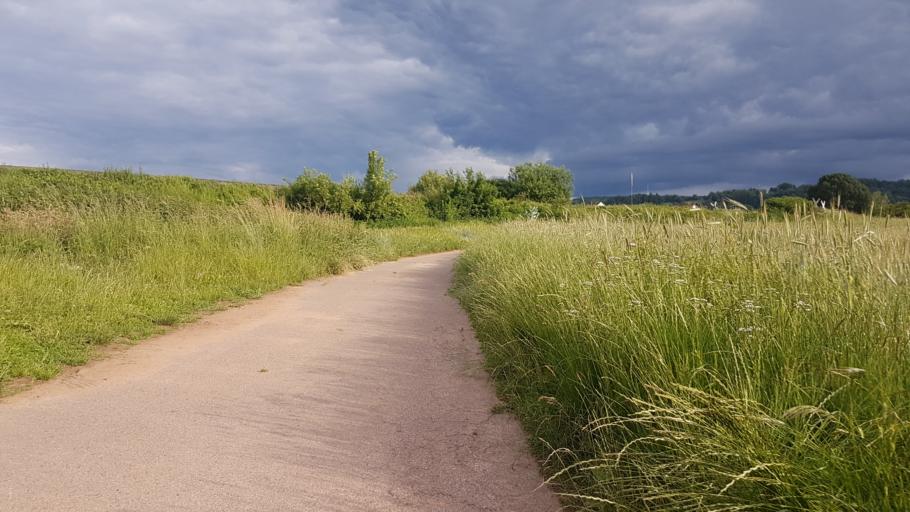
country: DE
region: Saarland
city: Britten
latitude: 49.4863
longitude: 6.7026
